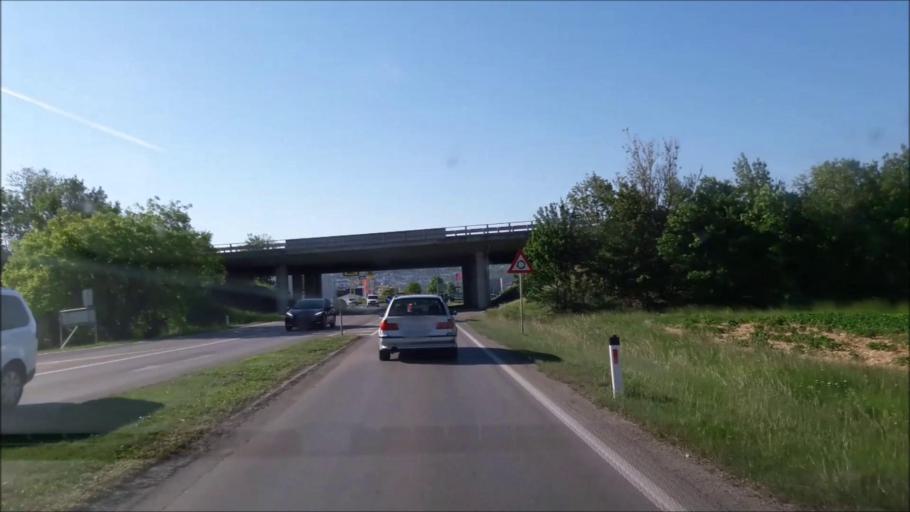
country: AT
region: Burgenland
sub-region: Eisenstadt Stadt
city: Eisenstadt
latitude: 47.8240
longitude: 16.5345
